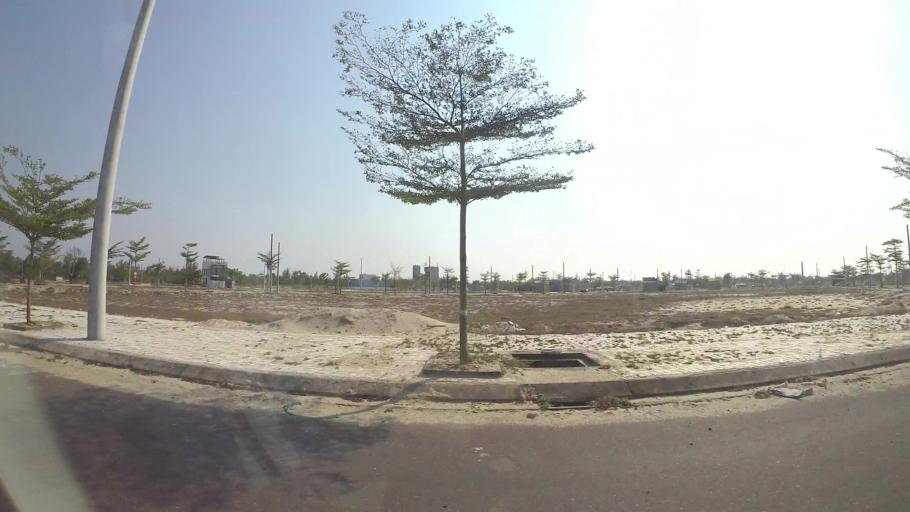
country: VN
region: Da Nang
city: Ngu Hanh Son
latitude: 15.9562
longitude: 108.2764
